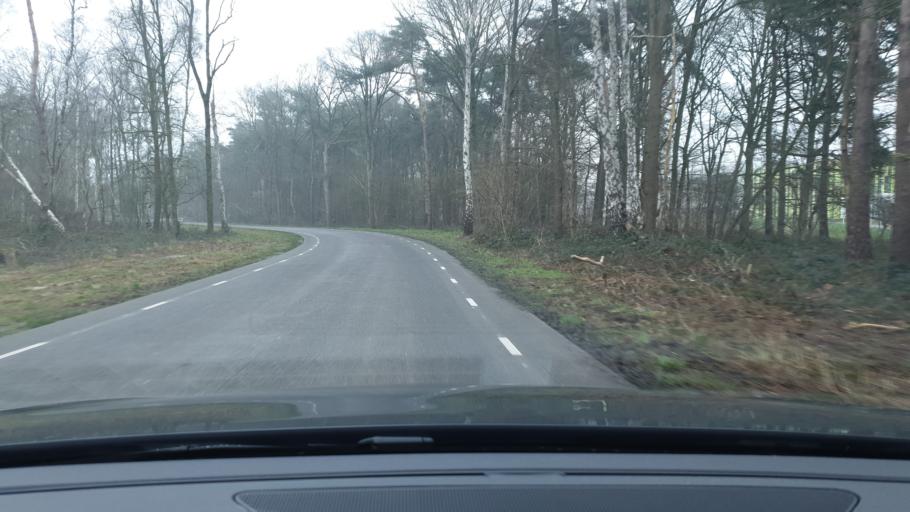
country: NL
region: North Brabant
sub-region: Gemeente Eindhoven
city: Meerhoven
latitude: 51.4613
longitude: 5.3990
